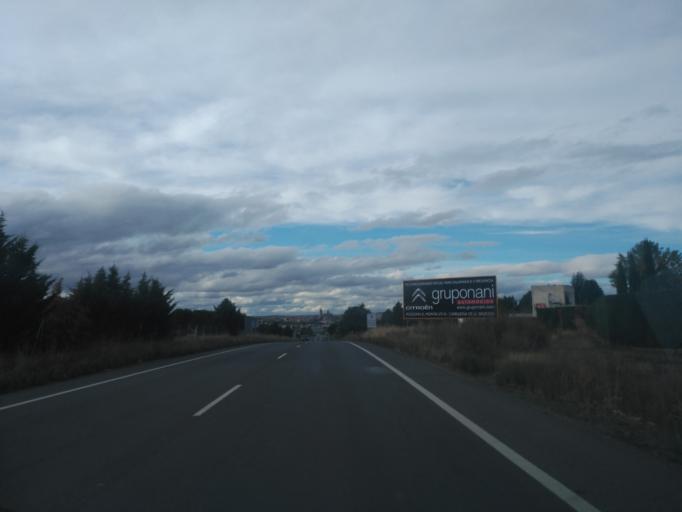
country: ES
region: Castille and Leon
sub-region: Provincia de Salamanca
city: Santa Marta de Tormes
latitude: 40.9371
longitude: -5.6315
